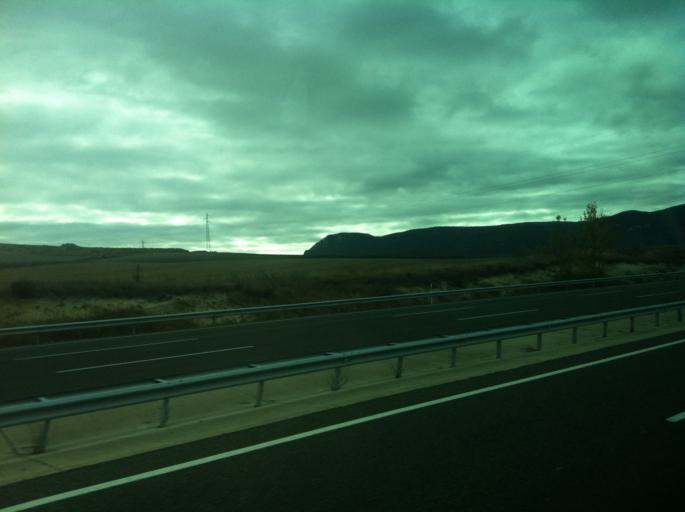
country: ES
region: Castille and Leon
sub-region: Provincia de Burgos
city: Bugedo
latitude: 42.6746
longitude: -3.0213
